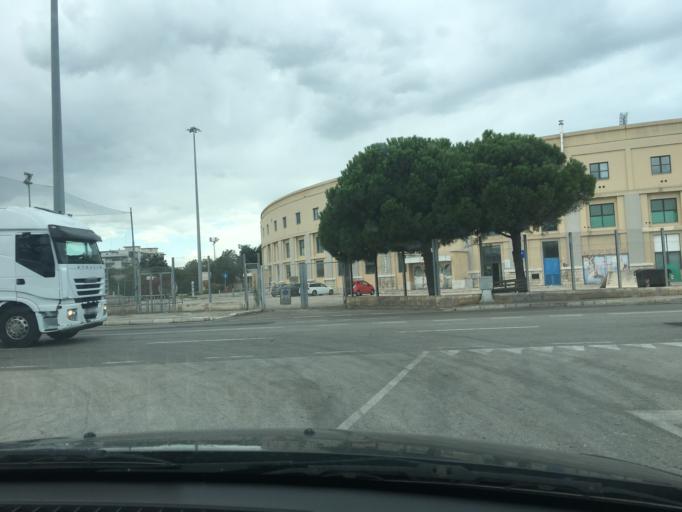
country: IT
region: Apulia
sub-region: Provincia di Bari
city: Bari
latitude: 41.1323
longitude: 16.8413
